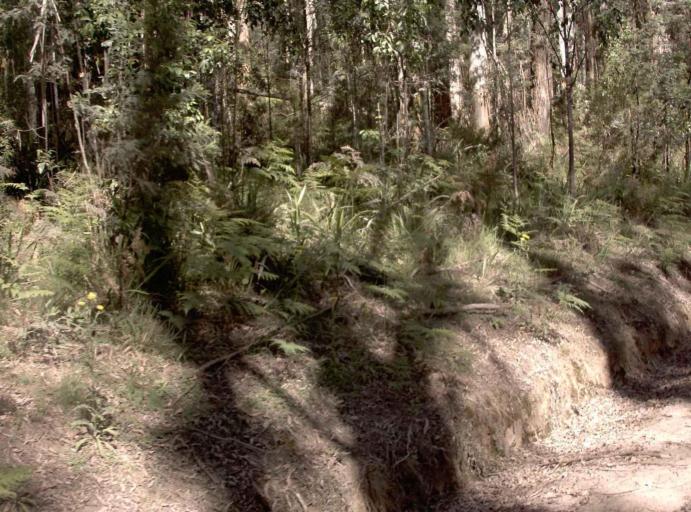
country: AU
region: New South Wales
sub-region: Bombala
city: Bombala
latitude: -37.2277
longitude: 148.7503
